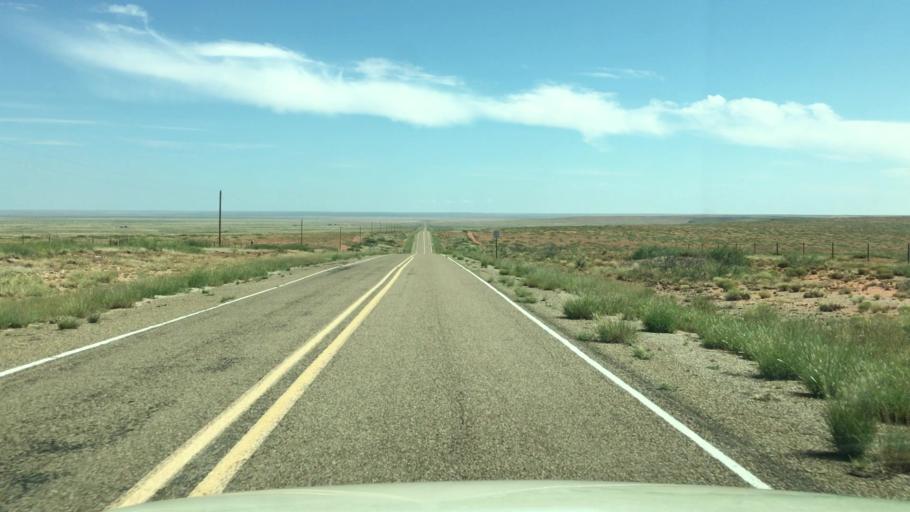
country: US
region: New Mexico
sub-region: Chaves County
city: Roswell
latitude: 33.9702
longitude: -104.5795
